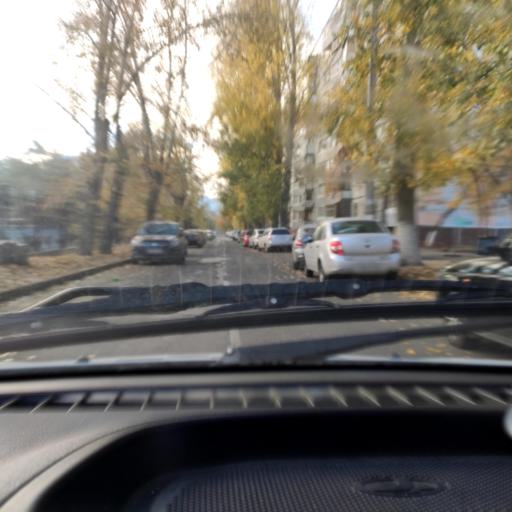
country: RU
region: Samara
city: Zhigulevsk
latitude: 53.4817
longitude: 49.4641
